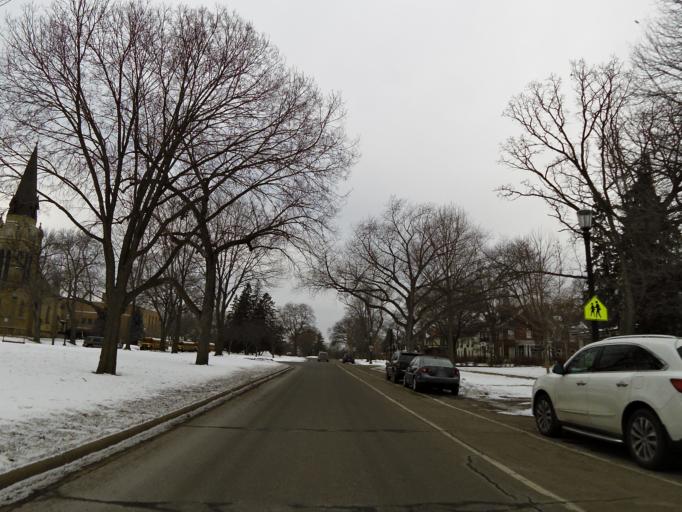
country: US
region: Minnesota
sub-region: Ramsey County
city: Falcon Heights
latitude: 44.9416
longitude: -93.1636
